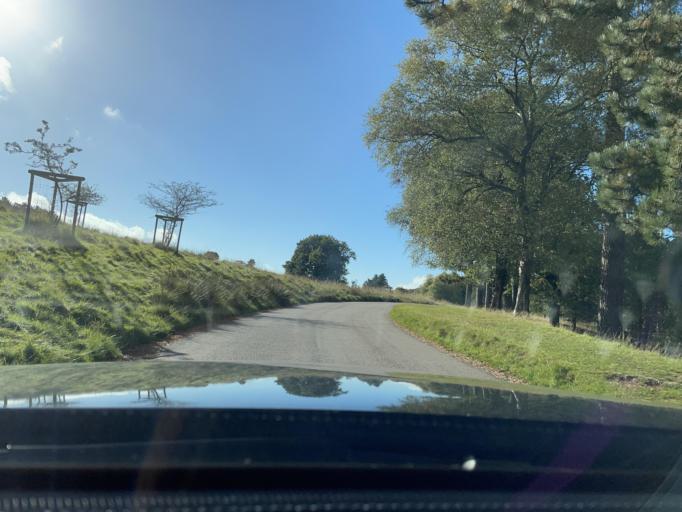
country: GB
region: England
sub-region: Cheshire East
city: Disley
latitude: 53.3501
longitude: -2.0544
